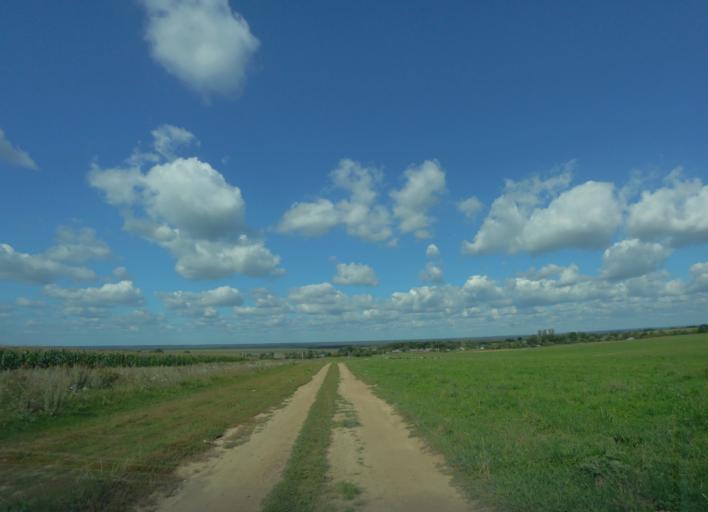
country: BY
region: Minsk
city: Zyembin
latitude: 54.3854
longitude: 28.3870
